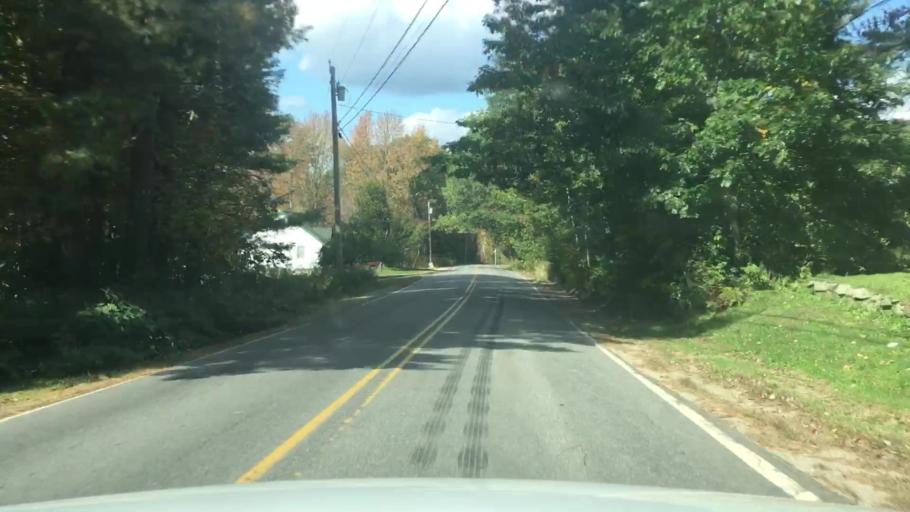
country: US
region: Maine
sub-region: Knox County
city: Warren
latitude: 44.1601
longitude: -69.2434
